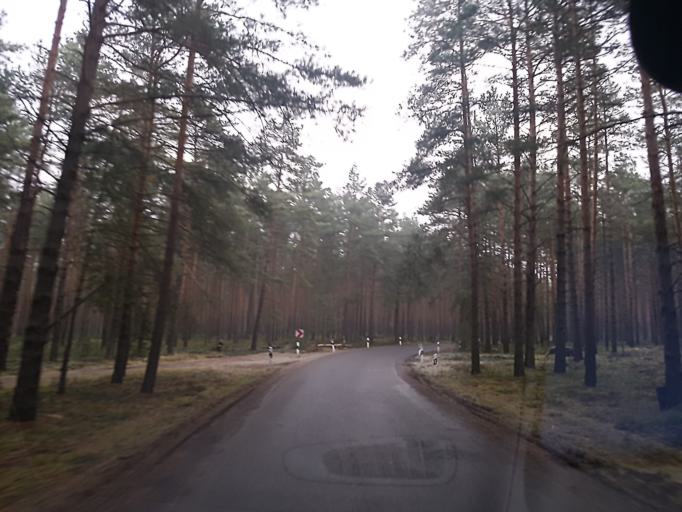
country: DE
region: Brandenburg
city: Crinitz
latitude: 51.7012
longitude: 13.7524
